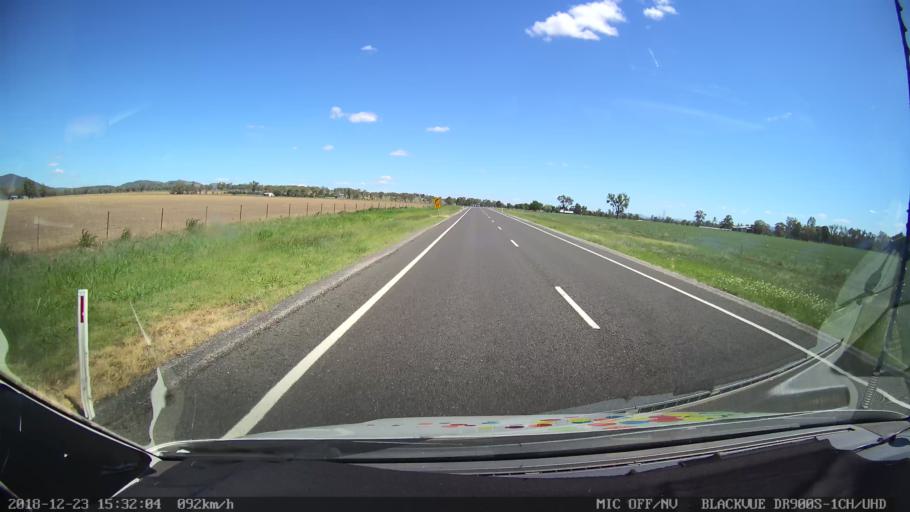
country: AU
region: New South Wales
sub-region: Tamworth Municipality
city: East Tamworth
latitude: -30.9810
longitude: 150.8701
